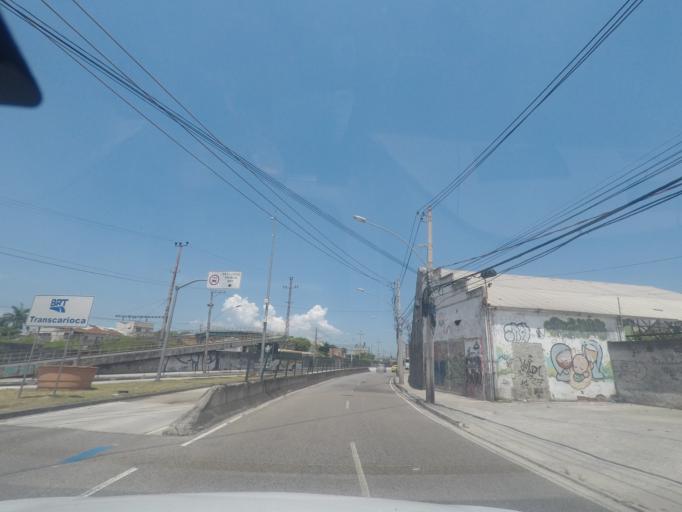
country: BR
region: Rio de Janeiro
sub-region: Duque De Caxias
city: Duque de Caxias
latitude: -22.8419
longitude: -43.2748
